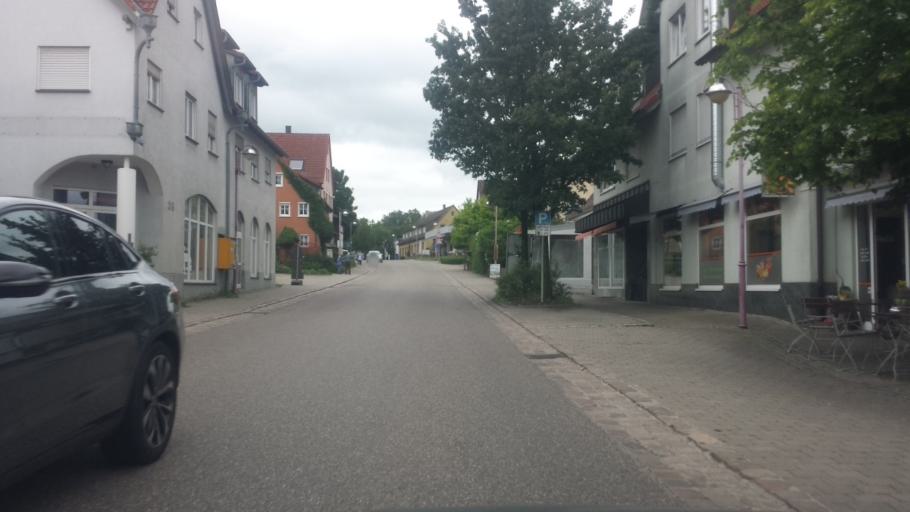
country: DE
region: Baden-Wuerttemberg
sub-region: Regierungsbezirk Stuttgart
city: Rot am See
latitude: 49.2514
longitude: 10.0257
